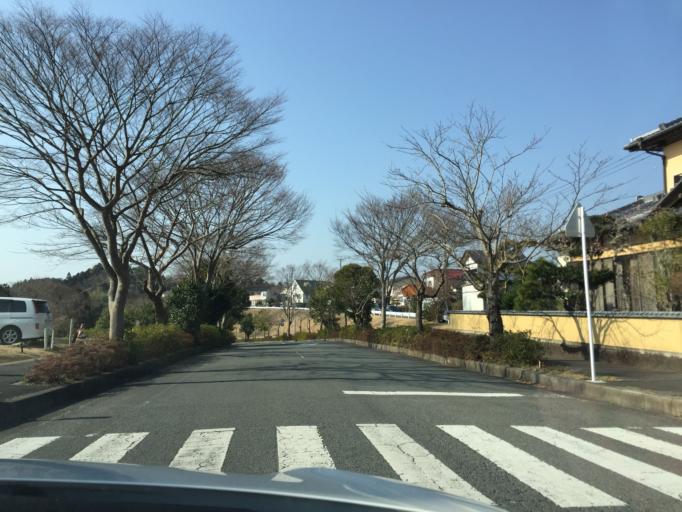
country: JP
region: Fukushima
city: Iwaki
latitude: 36.9645
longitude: 140.9341
